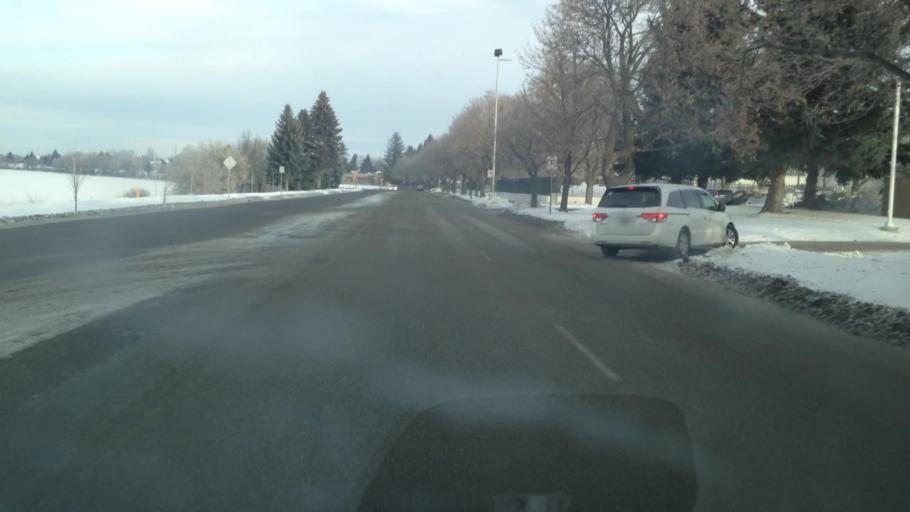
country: US
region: Idaho
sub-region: Bonneville County
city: Idaho Falls
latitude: 43.4984
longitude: -112.0419
